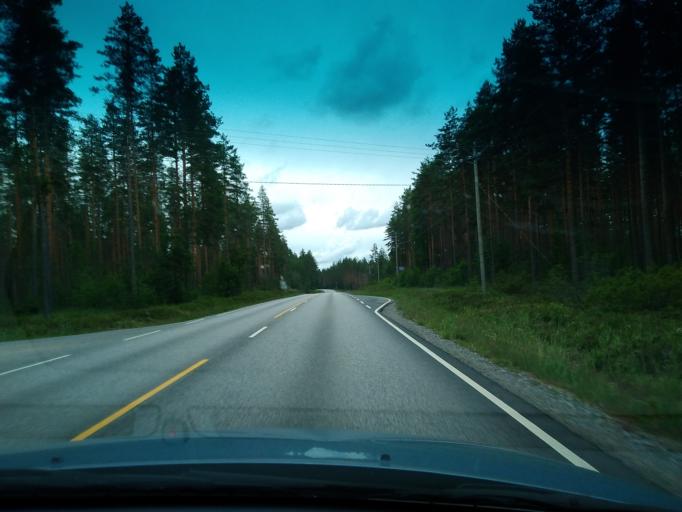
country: FI
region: Central Finland
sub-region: Keuruu
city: Multia
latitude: 62.4952
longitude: 24.6886
